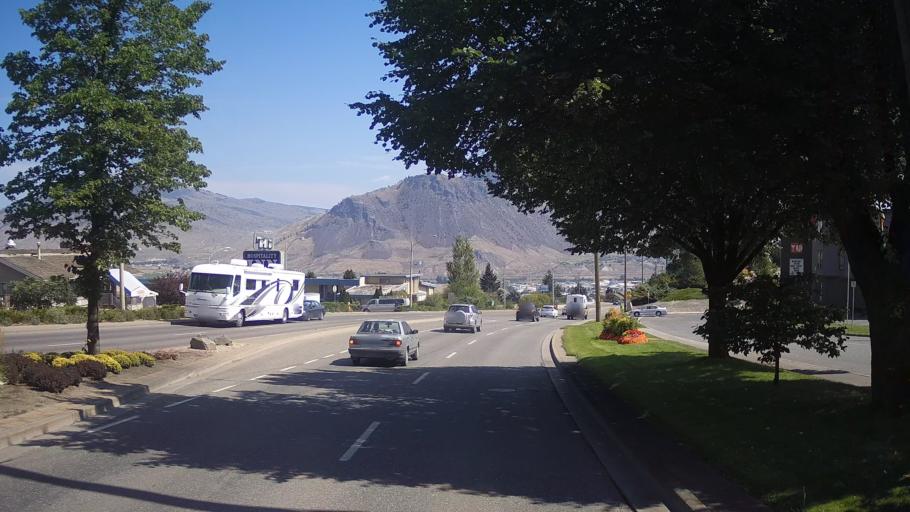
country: CA
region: British Columbia
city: Kamloops
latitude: 50.6727
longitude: -120.3530
